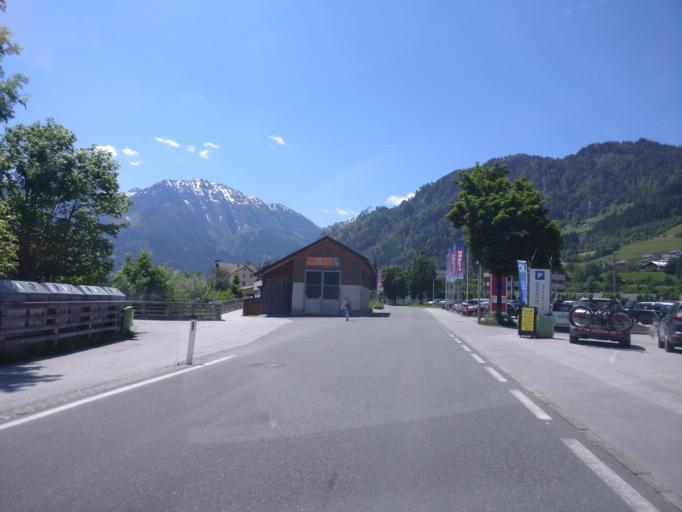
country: AT
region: Salzburg
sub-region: Politischer Bezirk Sankt Johann im Pongau
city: Sankt Johann im Pongau
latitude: 47.3510
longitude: 13.1969
